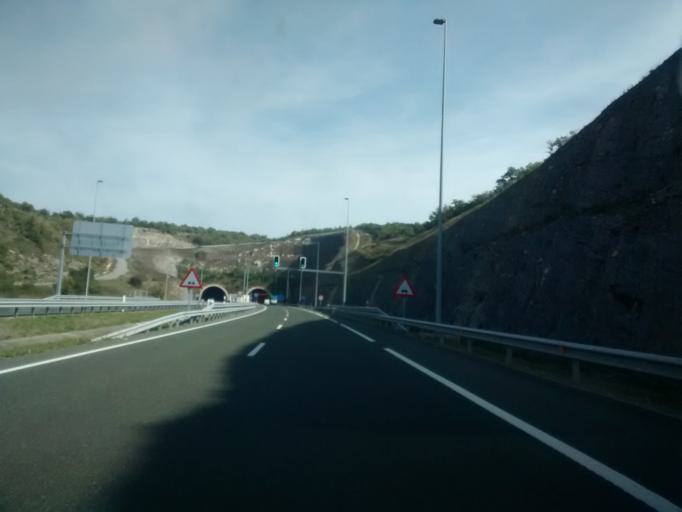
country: ES
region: Basque Country
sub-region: Provincia de Guipuzcoa
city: Leintz-Gatzaga
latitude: 42.9327
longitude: -2.6348
